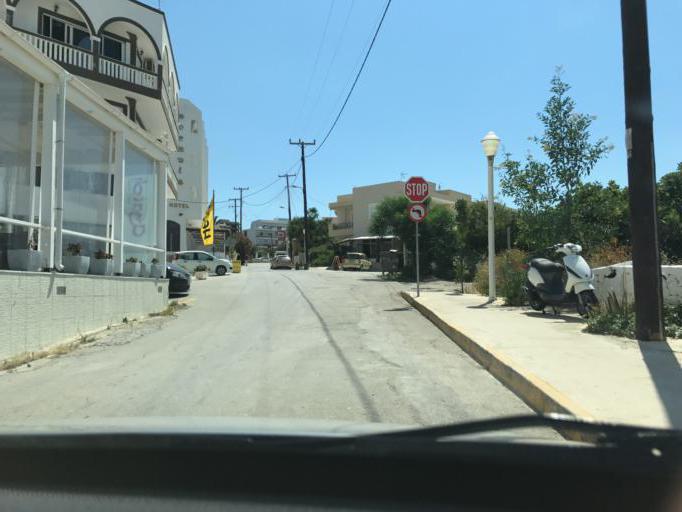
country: GR
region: South Aegean
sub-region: Nomos Dodekanisou
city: Karpathos
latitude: 35.5081
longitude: 27.2110
